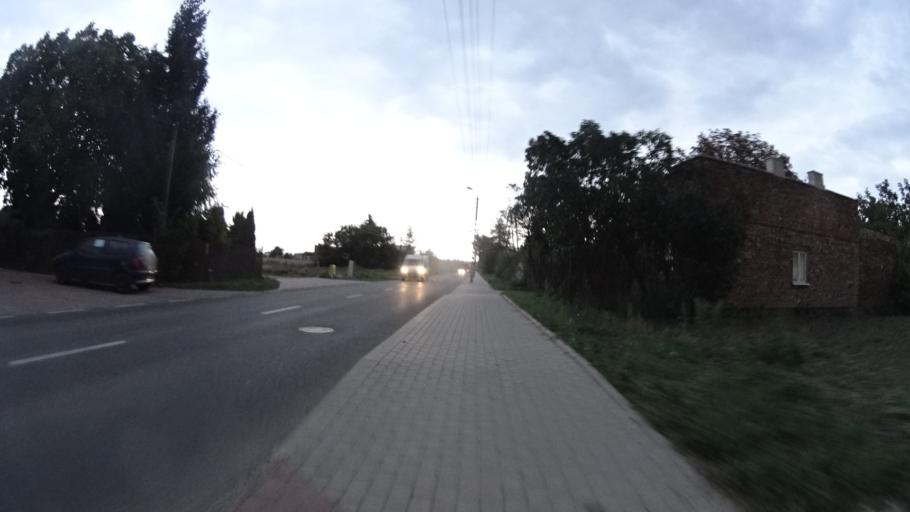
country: PL
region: Masovian Voivodeship
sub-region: Powiat warszawski zachodni
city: Babice
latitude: 52.2263
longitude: 20.8531
